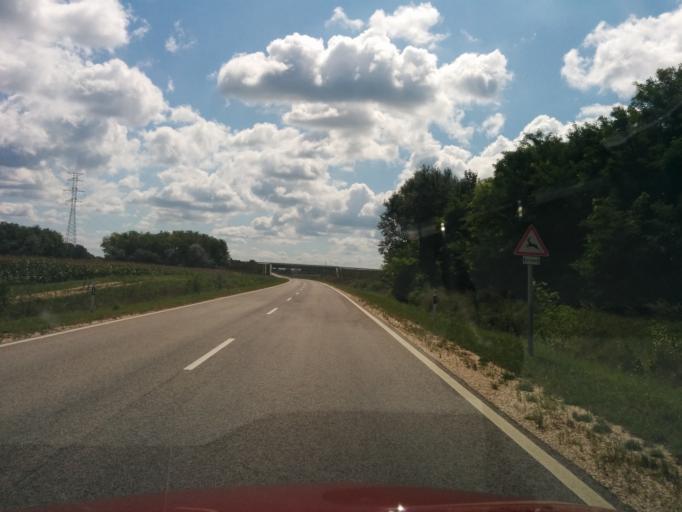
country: HU
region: Komarom-Esztergom
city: Komarom
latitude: 47.7327
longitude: 18.0991
